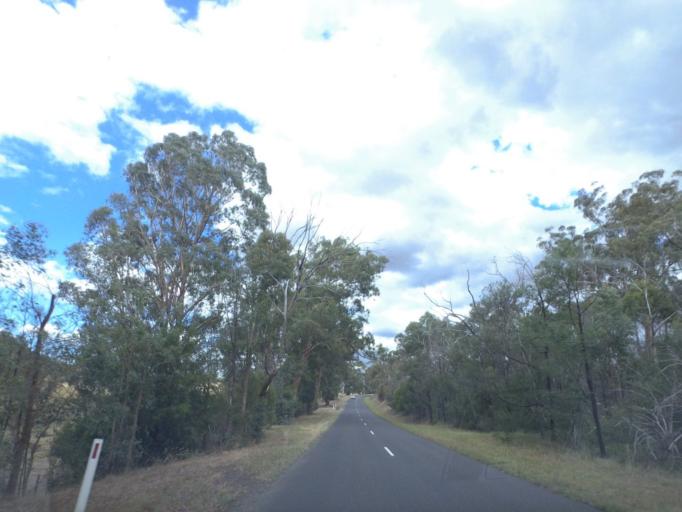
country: AU
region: Victoria
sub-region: Yarra Ranges
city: Healesville
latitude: -37.6427
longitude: 145.4529
